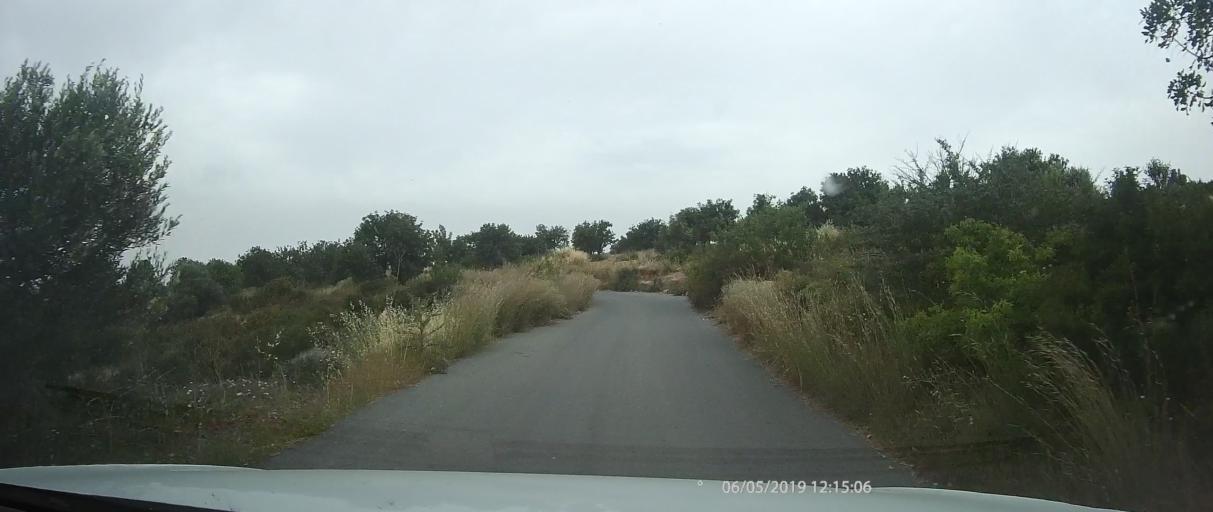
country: CY
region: Pafos
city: Tala
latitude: 34.8503
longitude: 32.4221
